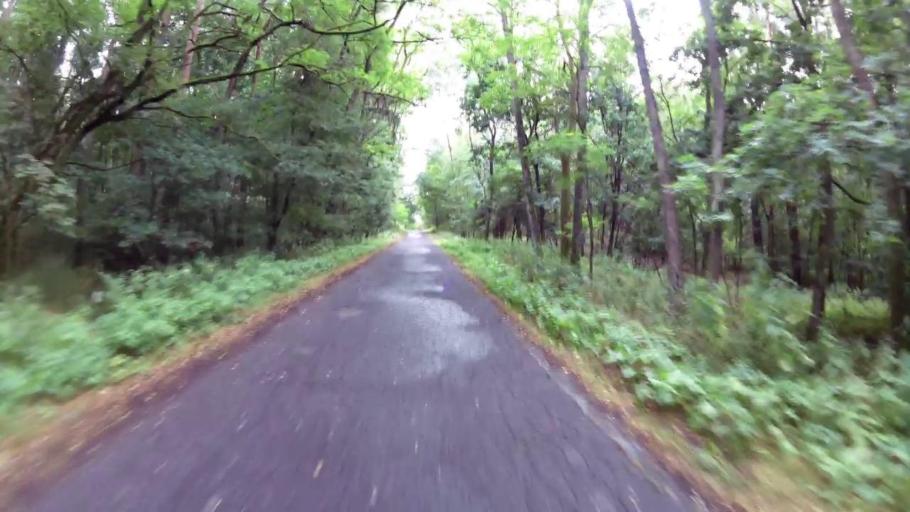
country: PL
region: West Pomeranian Voivodeship
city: Trzcinsko Zdroj
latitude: 52.8914
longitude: 14.7058
